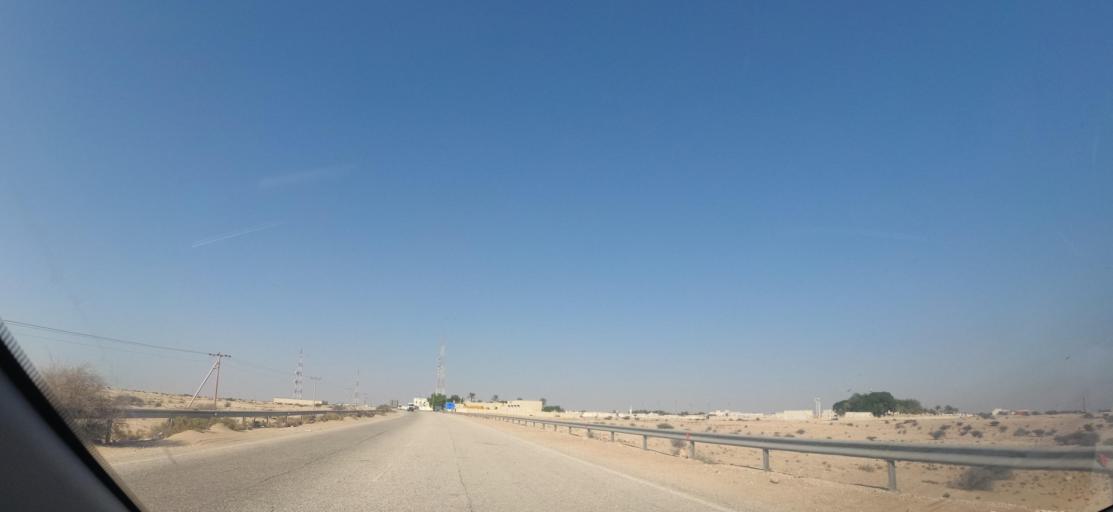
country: QA
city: Al Jumayliyah
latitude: 25.6144
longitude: 51.0788
